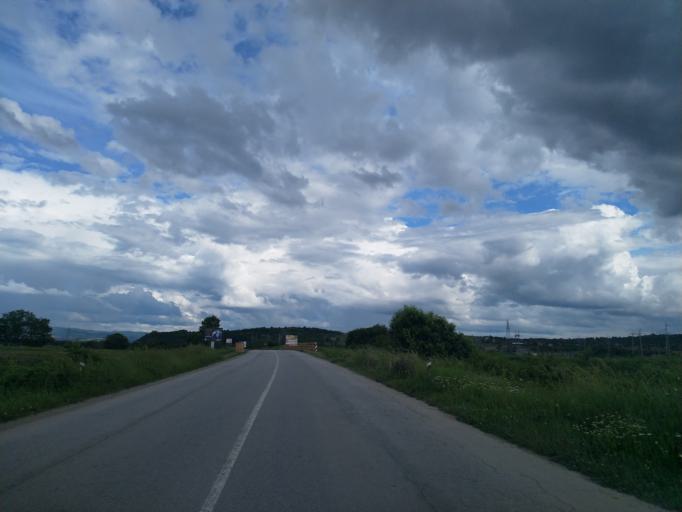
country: RS
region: Central Serbia
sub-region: Pomoravski Okrug
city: Jagodina
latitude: 43.9586
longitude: 21.2877
